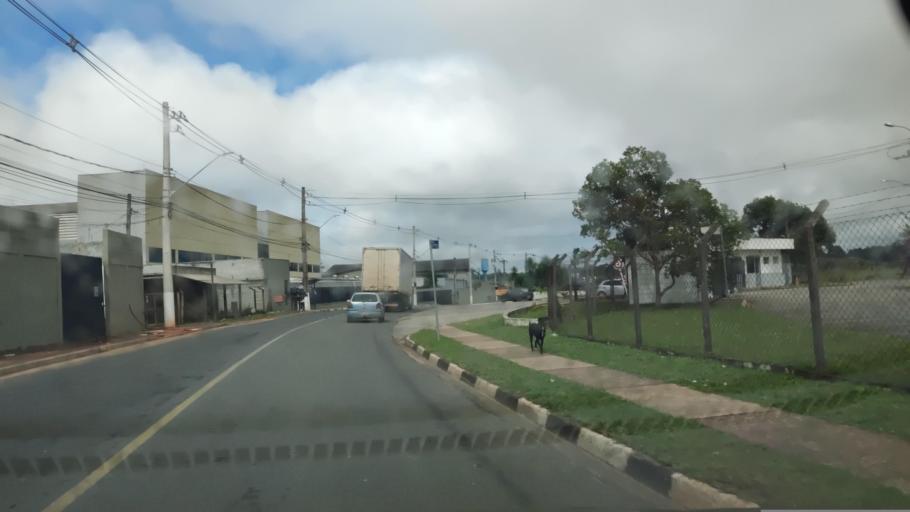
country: BR
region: Sao Paulo
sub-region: Vargem Grande Paulista
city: Vargem Grande Paulista
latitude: -23.6459
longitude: -47.0567
